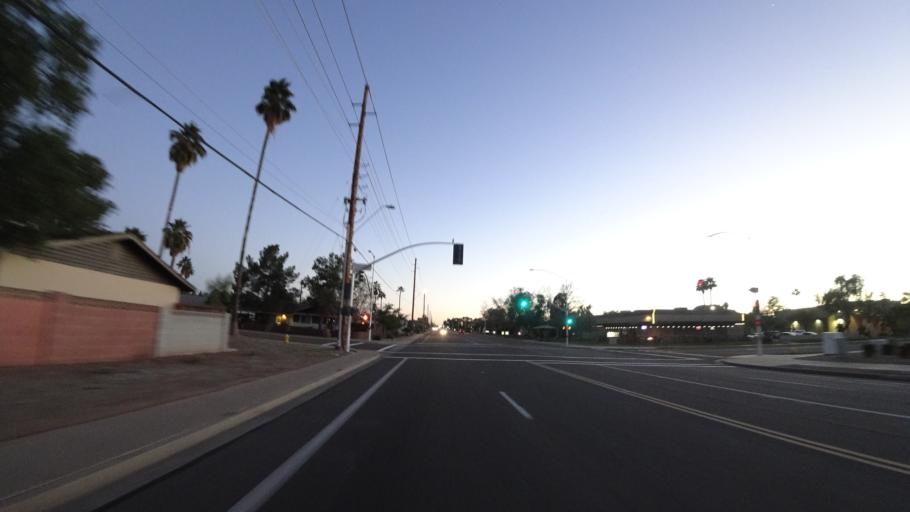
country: US
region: Arizona
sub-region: Maricopa County
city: Tempe Junction
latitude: 33.4134
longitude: -111.9608
